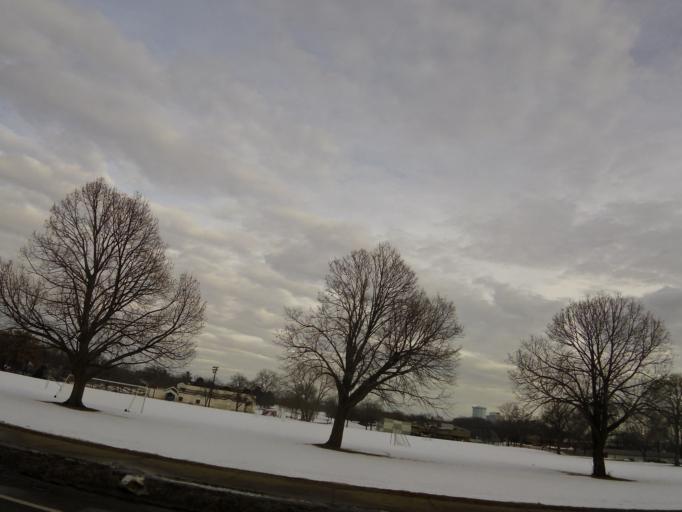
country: US
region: Minnesota
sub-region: Ramsey County
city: Maplewood
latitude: 44.9548
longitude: -93.0151
